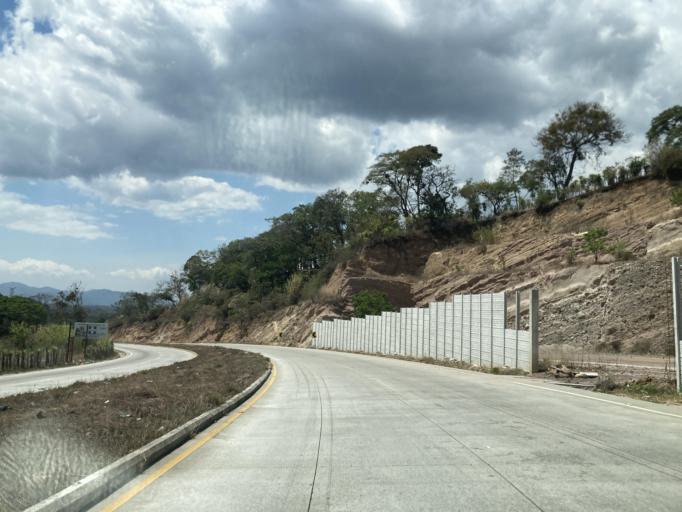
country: GT
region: Santa Rosa
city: Barberena
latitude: 14.3029
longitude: -90.3679
